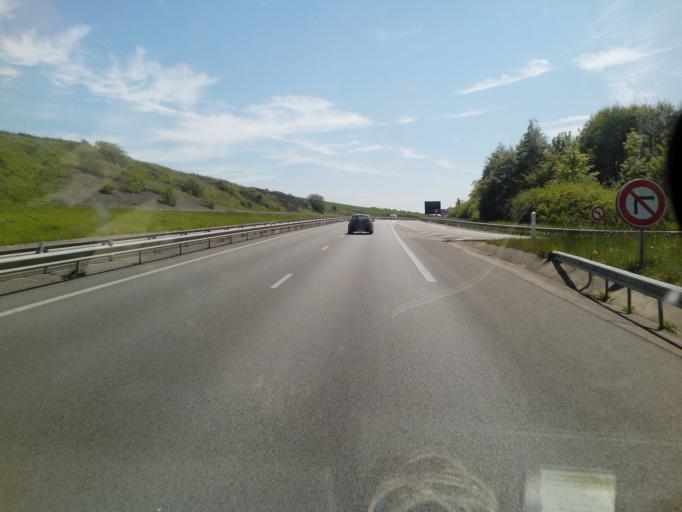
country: FR
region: Nord-Pas-de-Calais
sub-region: Departement du Pas-de-Calais
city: Saint-Martin-Boulogne
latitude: 50.7200
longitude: 1.6476
